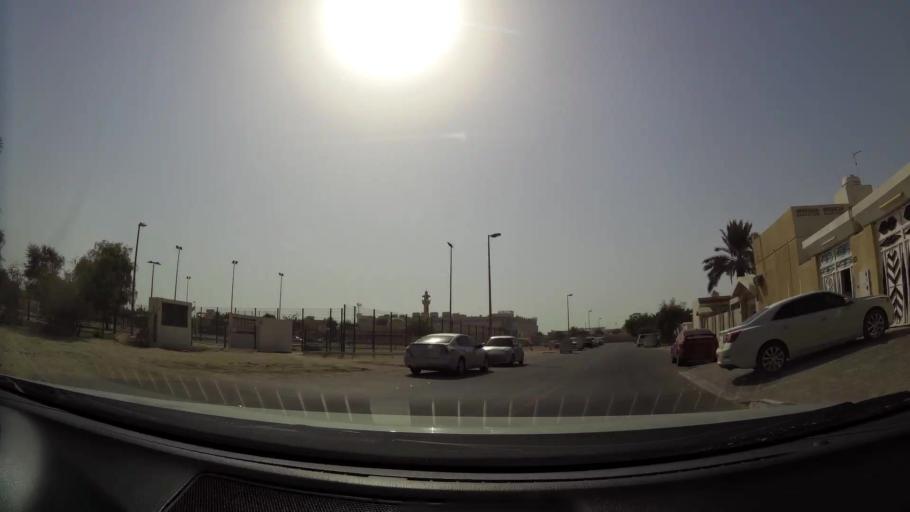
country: AE
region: Dubai
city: Dubai
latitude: 25.1682
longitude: 55.2466
